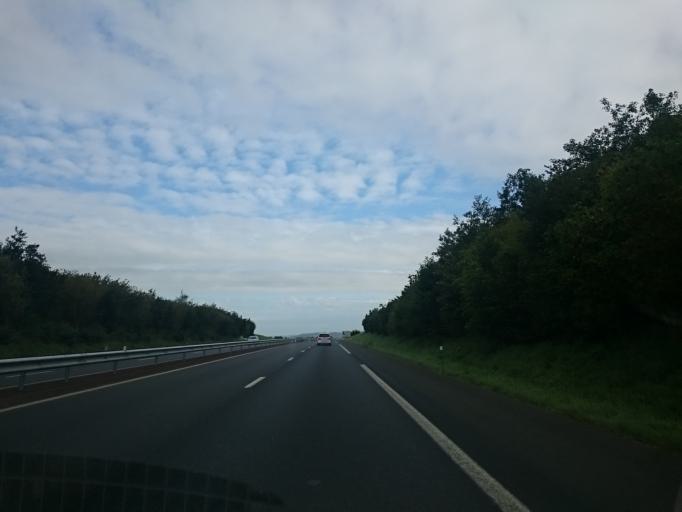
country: FR
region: Lower Normandy
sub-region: Departement de la Manche
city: Ducey
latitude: 48.6021
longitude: -1.3318
